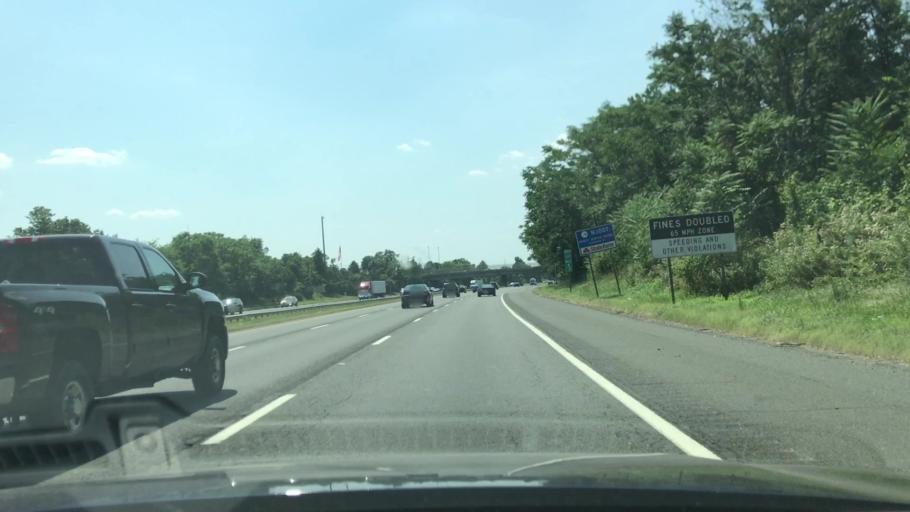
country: US
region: New Jersey
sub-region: Middlesex County
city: Society Hill
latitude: 40.5558
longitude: -74.4415
